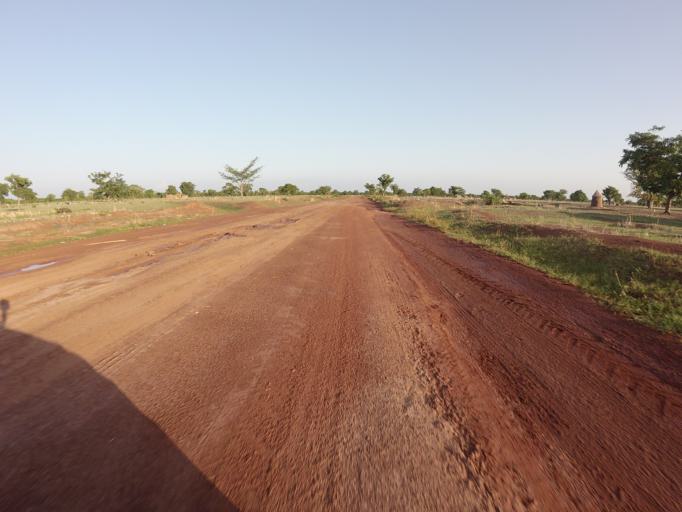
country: TG
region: Savanes
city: Sansanne-Mango
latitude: 10.2946
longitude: -0.0881
